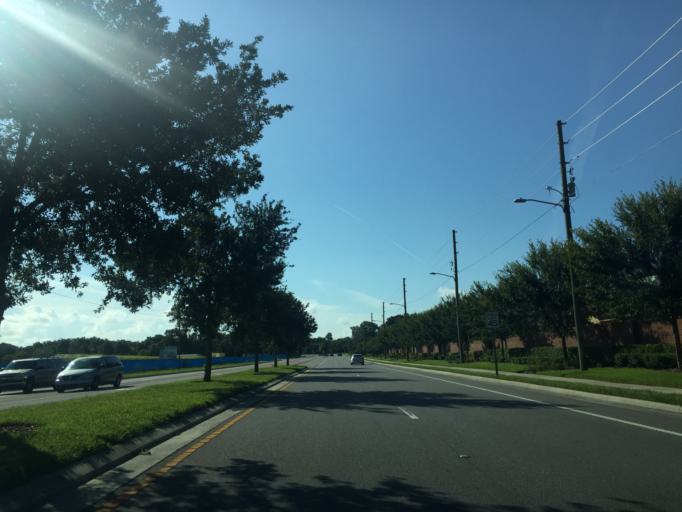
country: US
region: Florida
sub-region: Seminole County
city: Winter Springs
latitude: 28.6748
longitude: -81.3018
